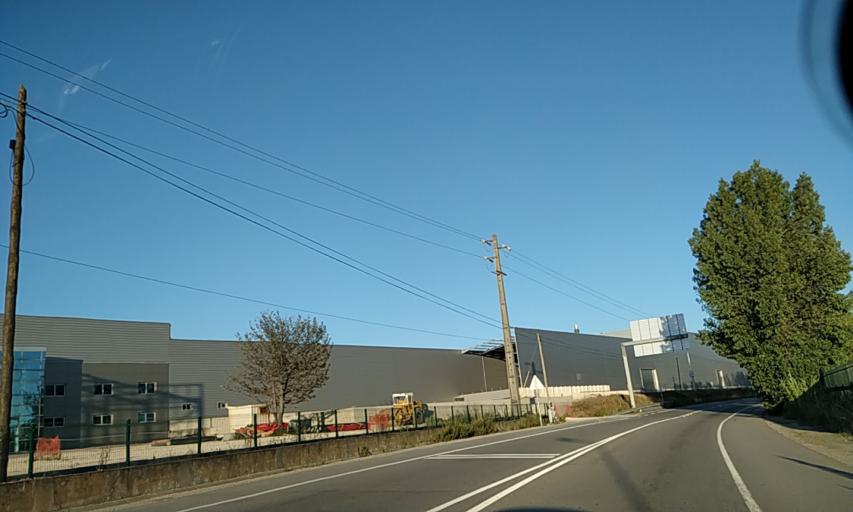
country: PT
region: Aveiro
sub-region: Oliveira do Bairro
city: Oia
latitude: 40.5561
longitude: -8.5535
